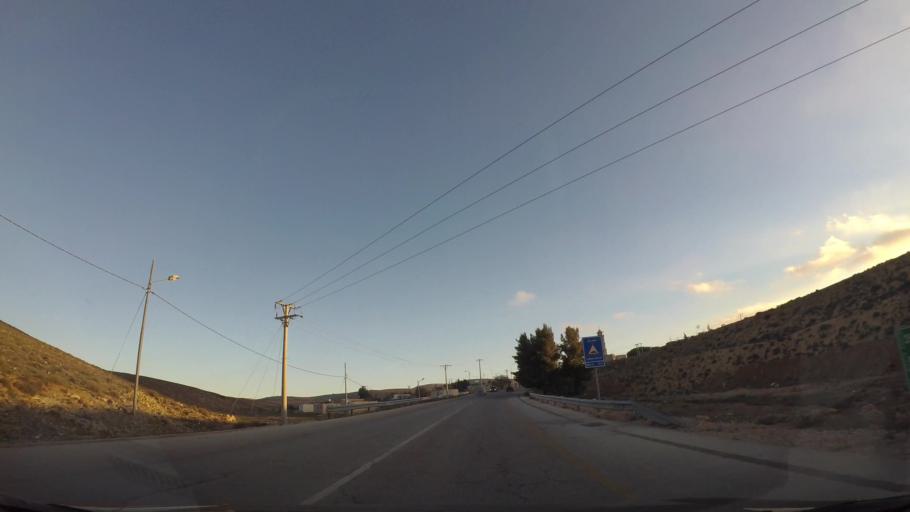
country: JO
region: Ma'an
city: Petra
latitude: 30.4537
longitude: 35.5256
